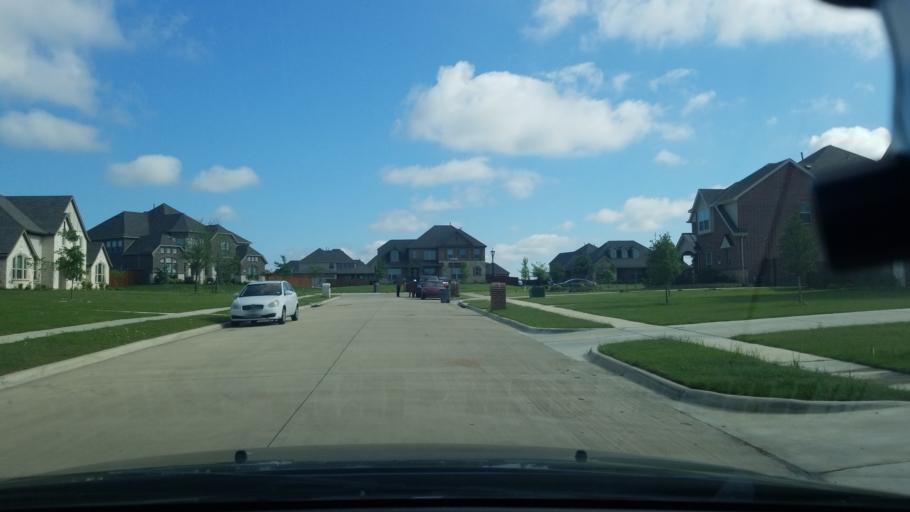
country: US
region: Texas
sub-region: Dallas County
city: Sunnyvale
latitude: 32.8010
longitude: -96.5675
